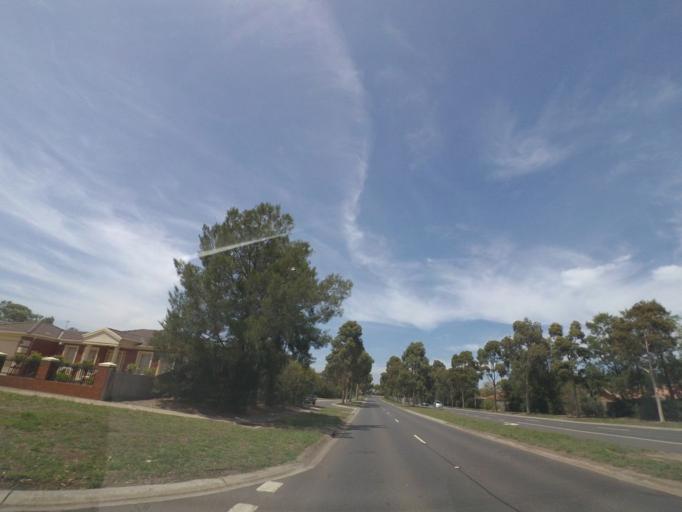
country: AU
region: Victoria
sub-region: Hume
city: Roxburgh Park
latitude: -37.6341
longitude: 144.9207
